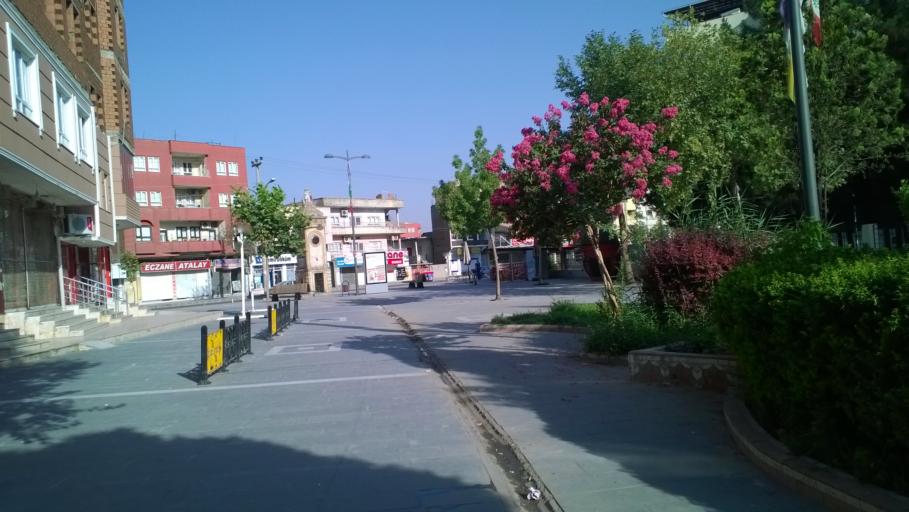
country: TR
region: Batman
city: Batman
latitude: 37.8878
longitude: 41.1260
